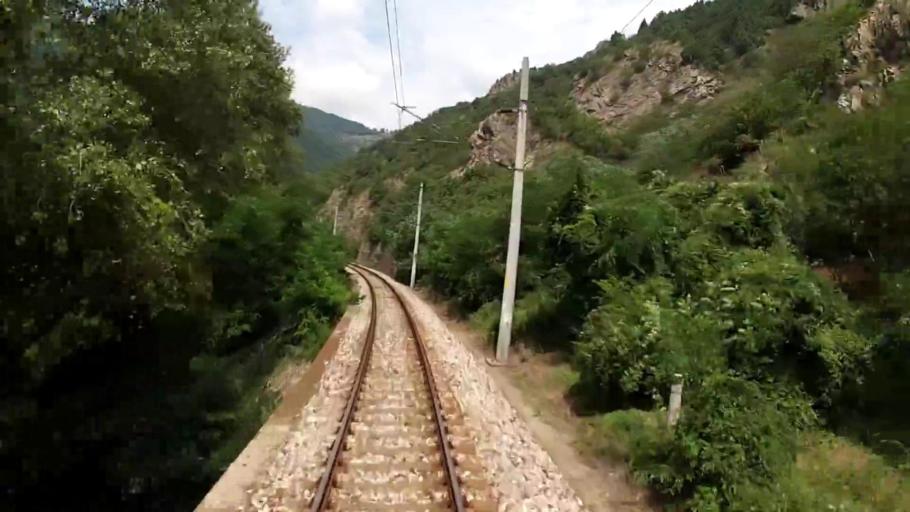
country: BG
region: Blagoevgrad
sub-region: Obshtina Kresna
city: Stara Kresna
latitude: 41.8131
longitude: 23.1621
